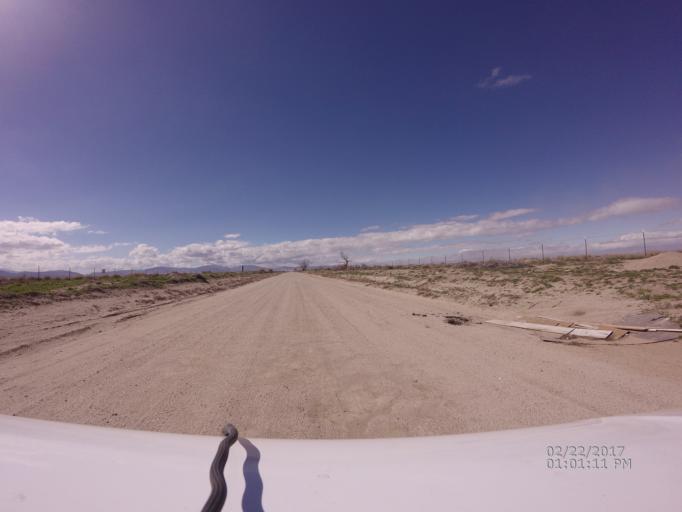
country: US
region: California
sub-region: Los Angeles County
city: Littlerock
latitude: 34.6019
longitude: -117.9607
